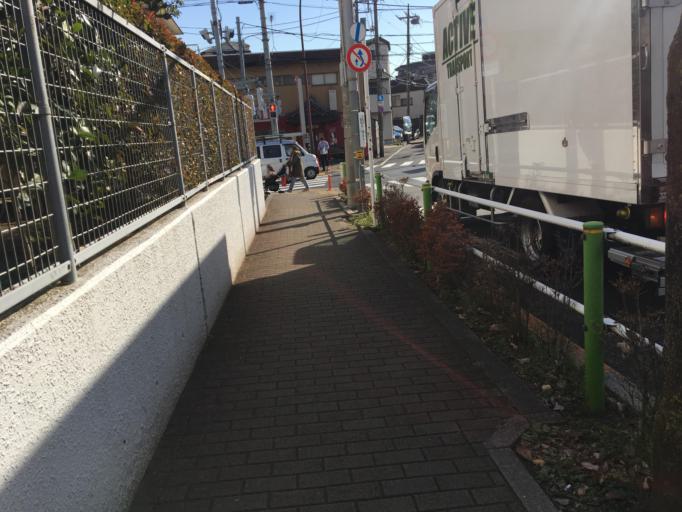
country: JP
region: Saitama
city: Wako
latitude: 35.7777
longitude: 139.6416
